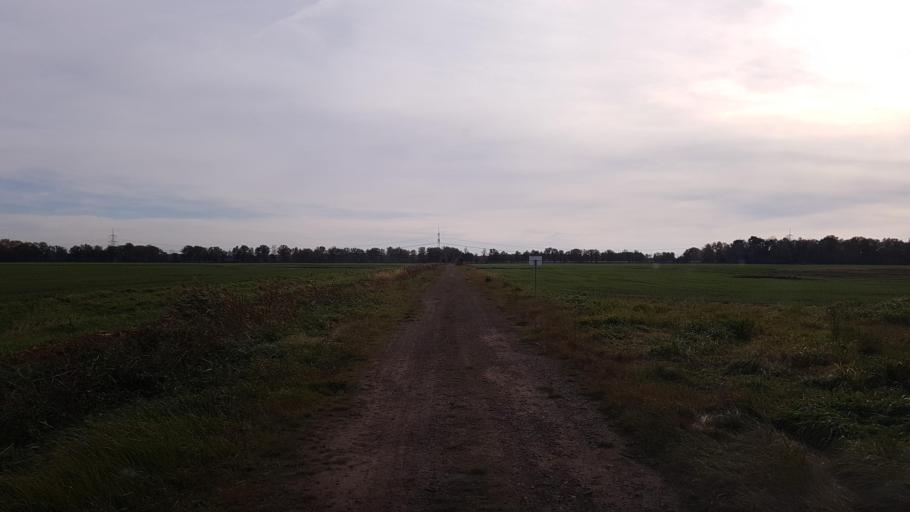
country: DE
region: Brandenburg
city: Schraden
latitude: 51.4592
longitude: 13.6907
